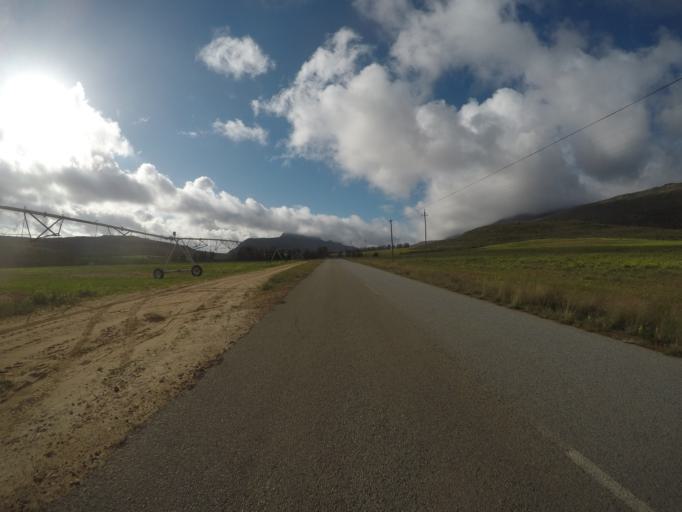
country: ZA
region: Western Cape
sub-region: West Coast District Municipality
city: Clanwilliam
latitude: -32.3446
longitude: 18.8402
